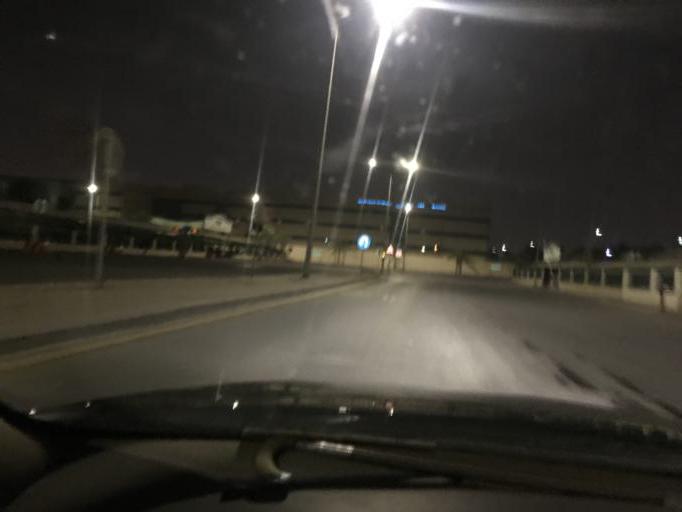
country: SA
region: Ar Riyad
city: Riyadh
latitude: 24.7970
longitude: 46.7096
